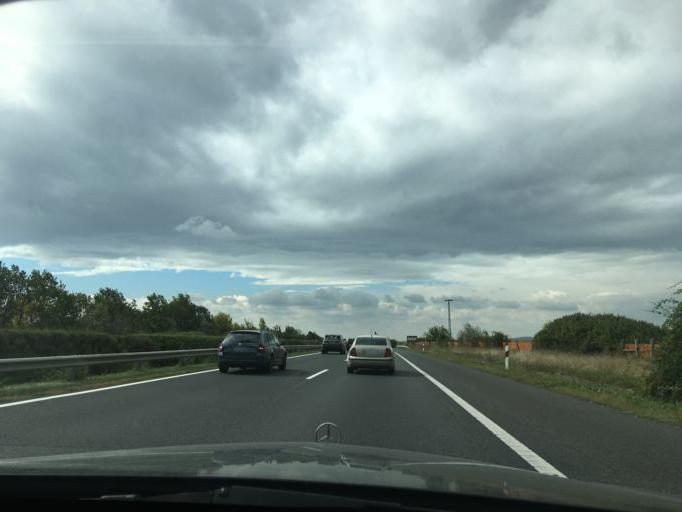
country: HU
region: Fejer
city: Martonvasar
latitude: 47.3499
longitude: 18.7992
